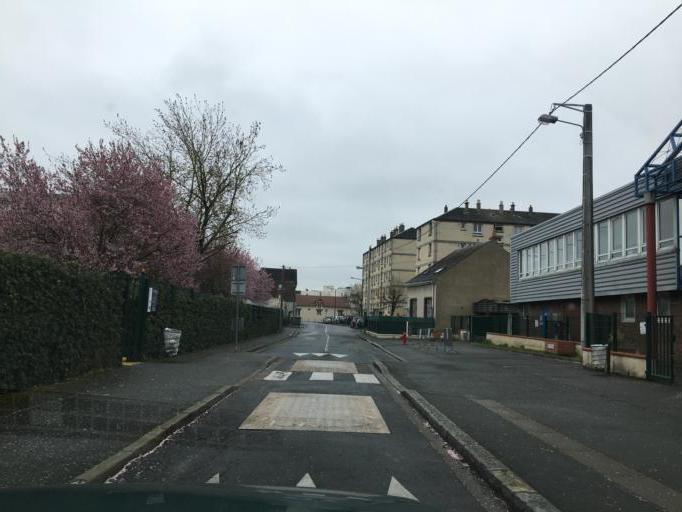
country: FR
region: Centre
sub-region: Departement du Loiret
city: Fleury-les-Aubrais
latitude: 47.9180
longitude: 1.9288
